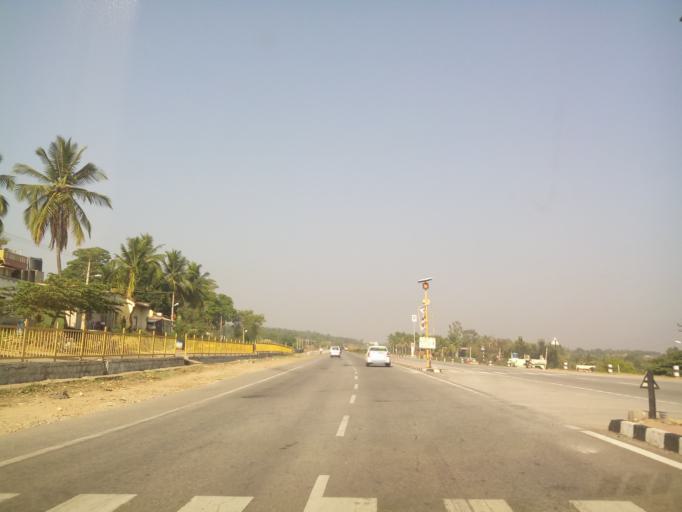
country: IN
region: Karnataka
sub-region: Bangalore Rural
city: Nelamangala
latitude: 13.0665
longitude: 77.3191
